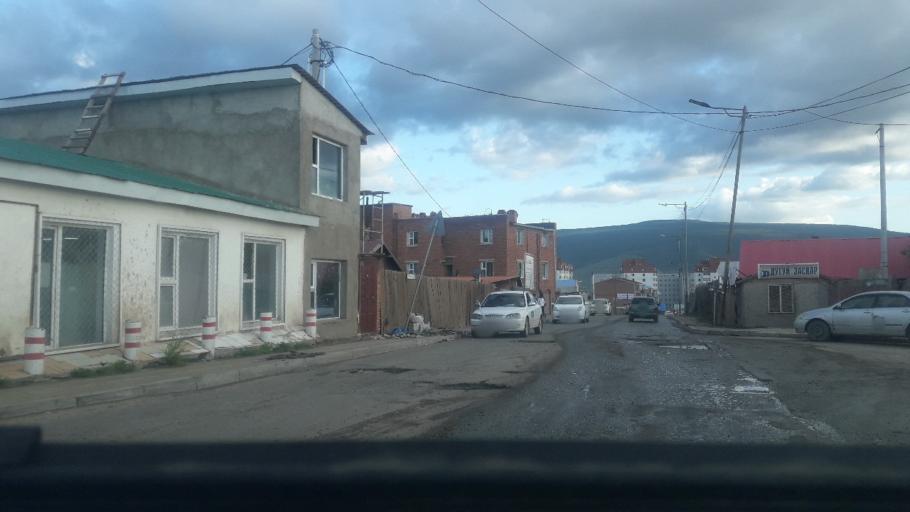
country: MN
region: Ulaanbaatar
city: Ulaanbaatar
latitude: 47.9212
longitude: 106.9954
